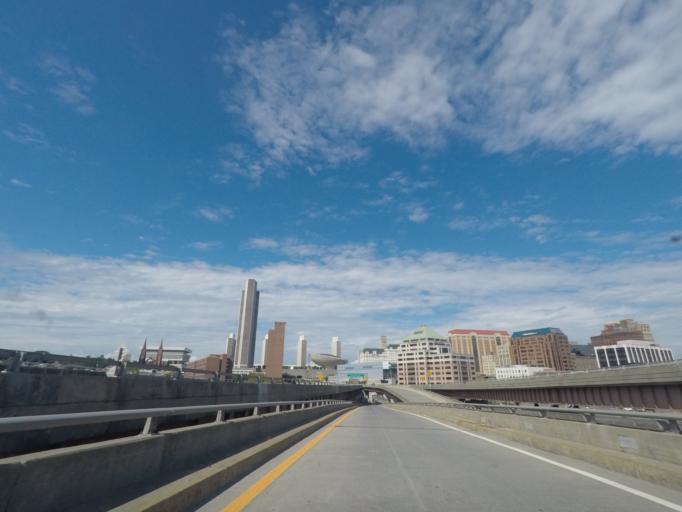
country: US
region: New York
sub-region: Albany County
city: Albany
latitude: 42.6452
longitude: -73.7520
